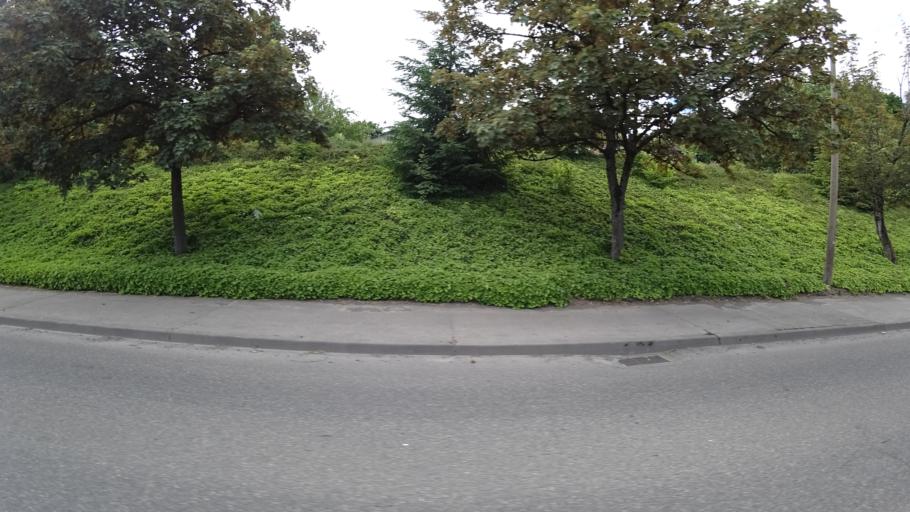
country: US
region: Oregon
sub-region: Washington County
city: West Haven
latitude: 45.6046
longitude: -122.7516
